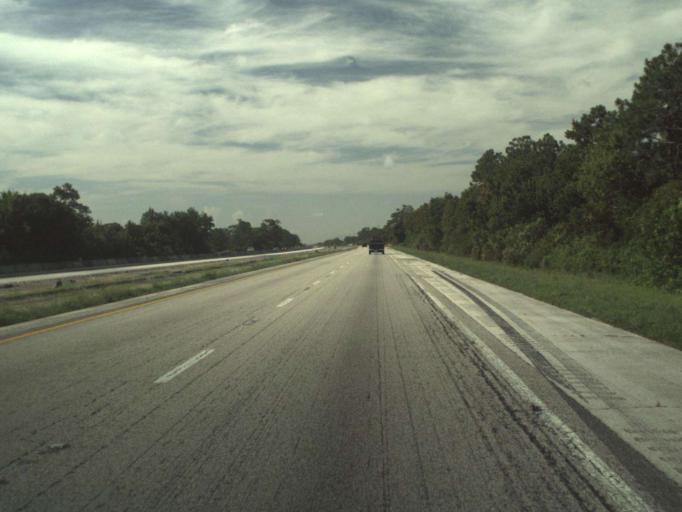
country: US
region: Florida
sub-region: Indian River County
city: Fellsmere
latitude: 27.7100
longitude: -80.5427
